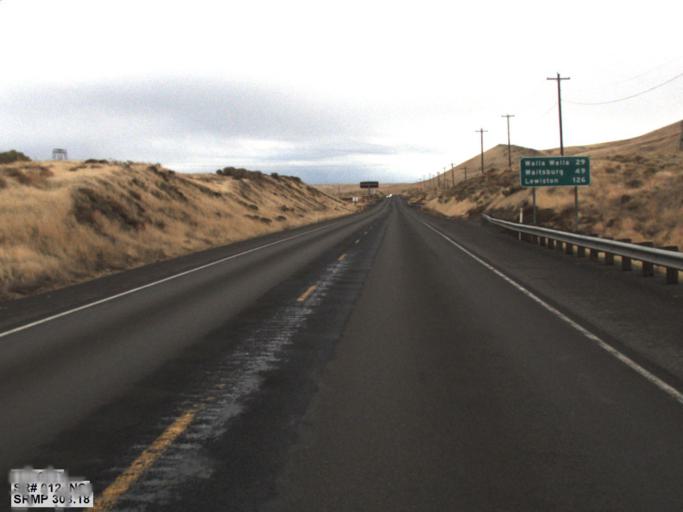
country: US
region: Washington
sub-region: Benton County
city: Finley
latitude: 46.0550
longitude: -118.8969
